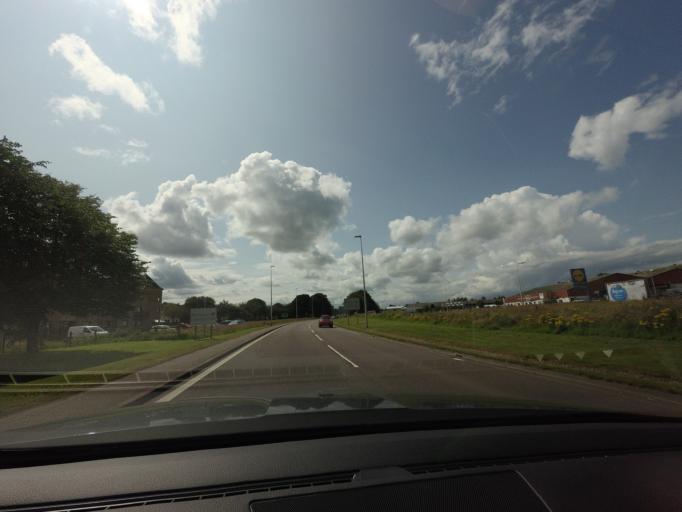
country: GB
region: Scotland
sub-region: Moray
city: Forres
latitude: 57.6072
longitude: -3.6307
